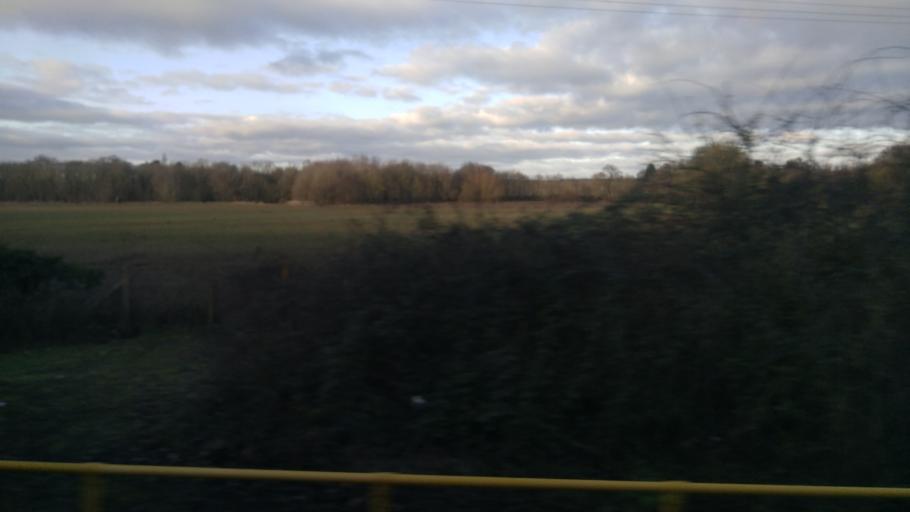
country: GB
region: England
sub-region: Kent
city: Headcorn
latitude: 51.1672
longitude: 0.6079
